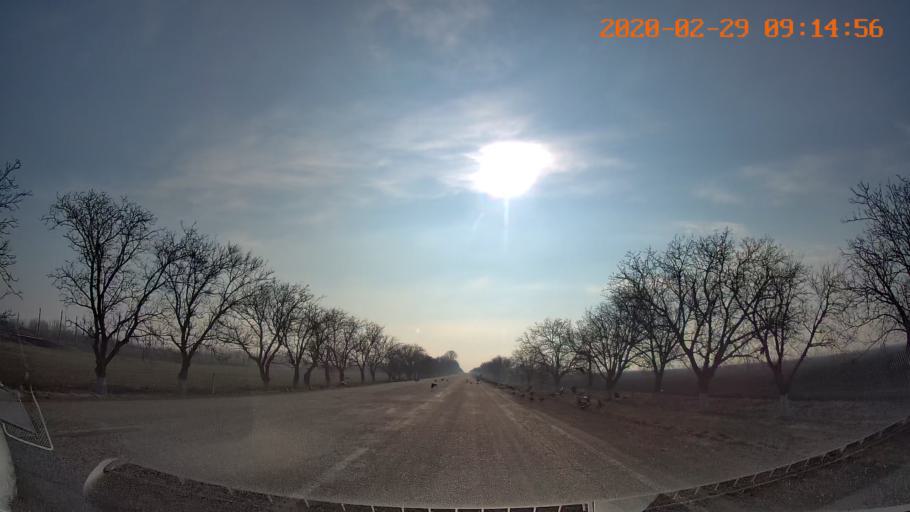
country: MD
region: Telenesti
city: Pervomaisc
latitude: 46.8045
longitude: 29.8610
